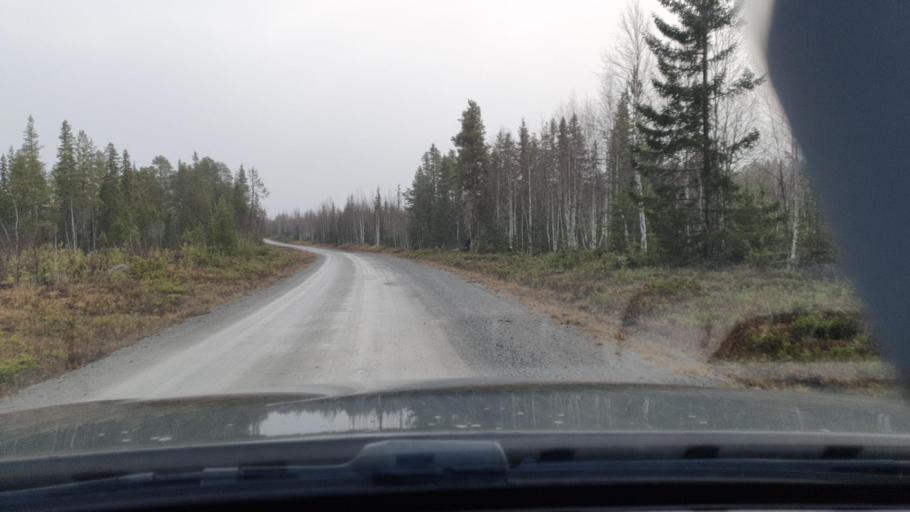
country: SE
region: Jaemtland
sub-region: Stroemsunds Kommun
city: Stroemsund
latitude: 63.5482
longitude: 15.5553
